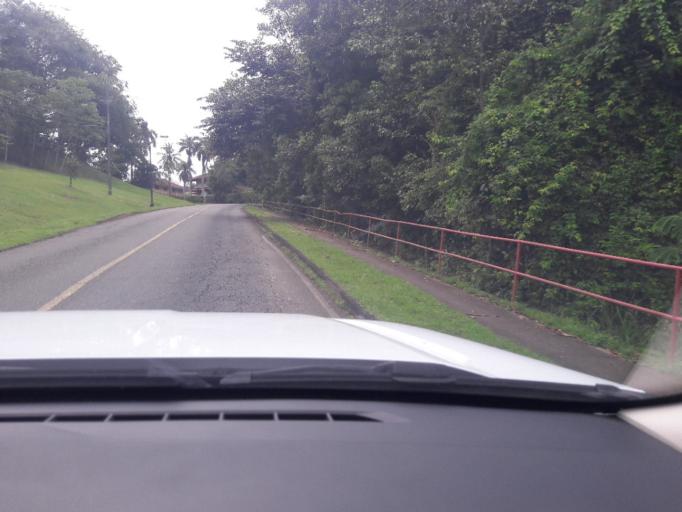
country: PA
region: Panama
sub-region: Distrito de Panama
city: Ancon
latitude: 9.0073
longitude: -79.5742
